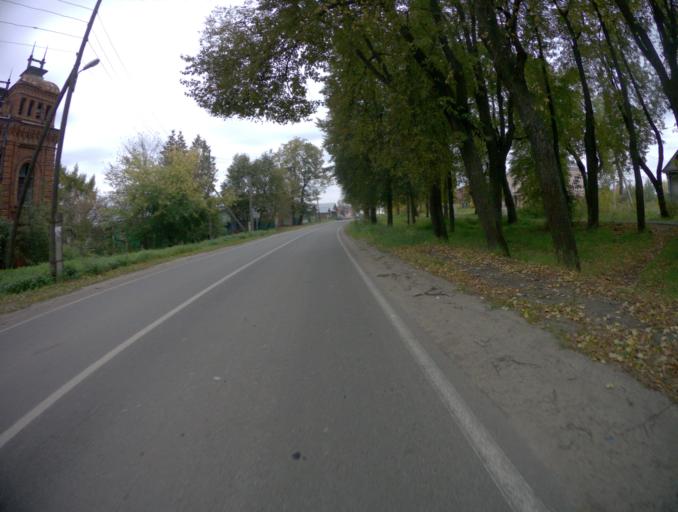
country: RU
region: Vladimir
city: Mstera
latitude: 56.3788
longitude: 41.9330
